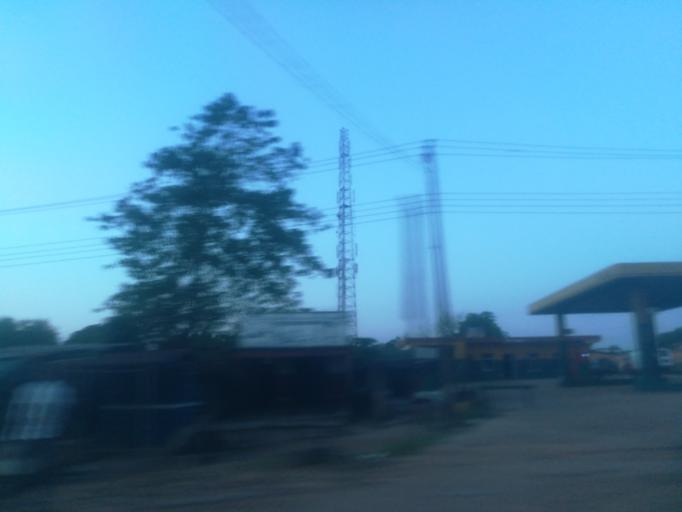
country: NG
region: Ogun
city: Abeokuta
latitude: 7.1800
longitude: 3.4118
